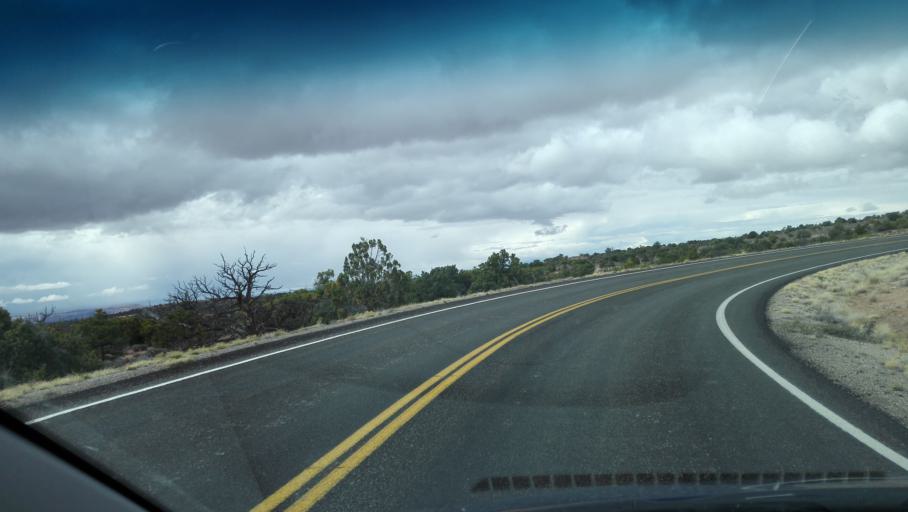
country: US
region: Utah
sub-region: Grand County
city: Moab
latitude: 38.3402
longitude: -109.8607
